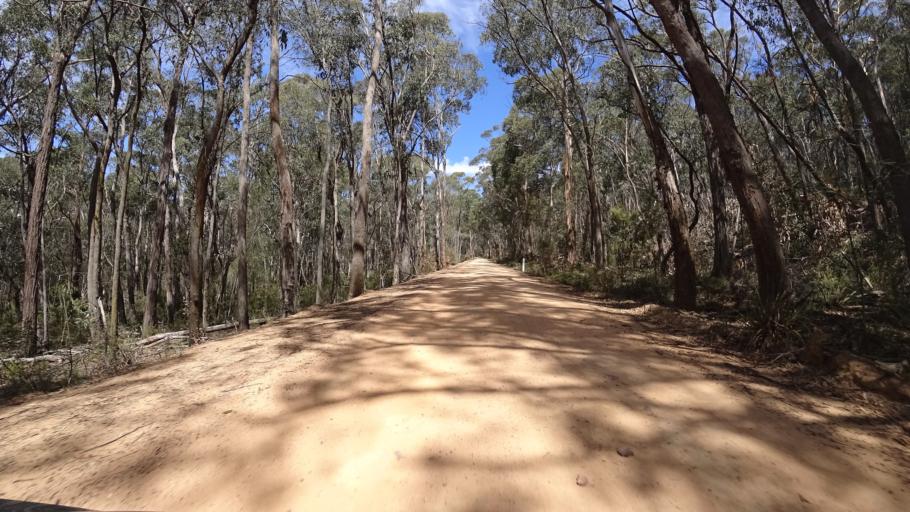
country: AU
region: New South Wales
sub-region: Lithgow
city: Lithgow
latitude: -33.2642
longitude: 150.2246
